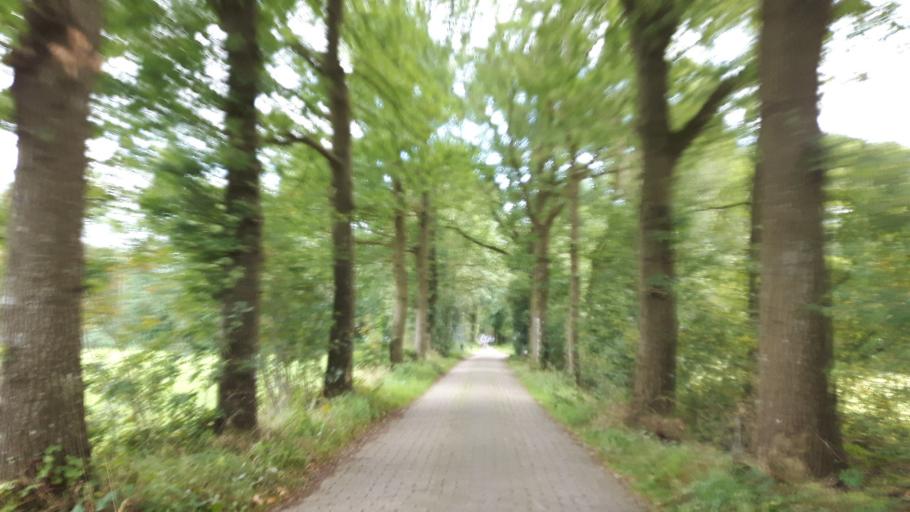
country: NL
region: Friesland
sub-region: Gemeente Smallingerland
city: Drachtstercompagnie
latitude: 53.0640
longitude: 6.2201
